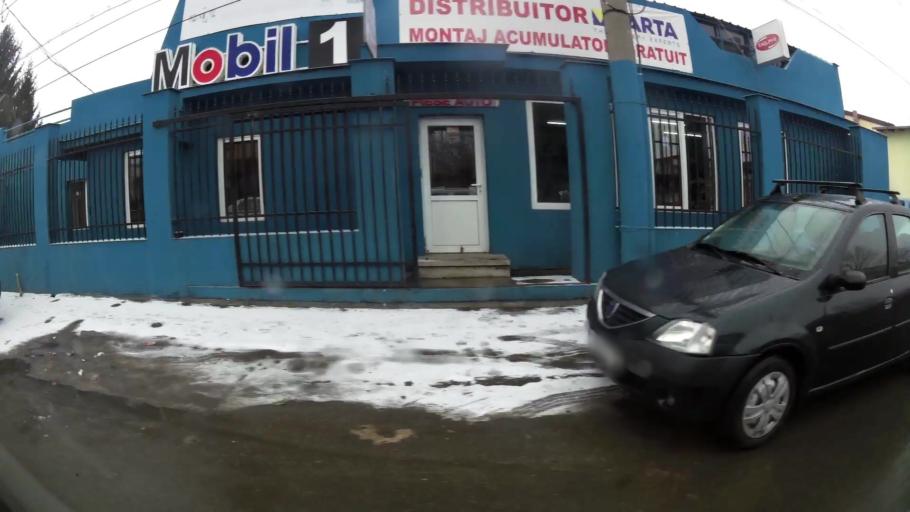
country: RO
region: Prahova
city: Ploiesti
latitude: 44.9540
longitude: 26.0167
